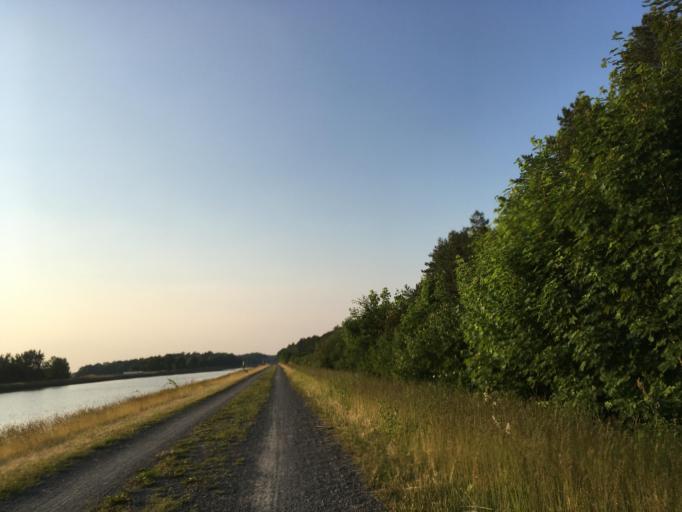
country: DE
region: Lower Saxony
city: Wendisch Evern
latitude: 53.2587
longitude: 10.4860
